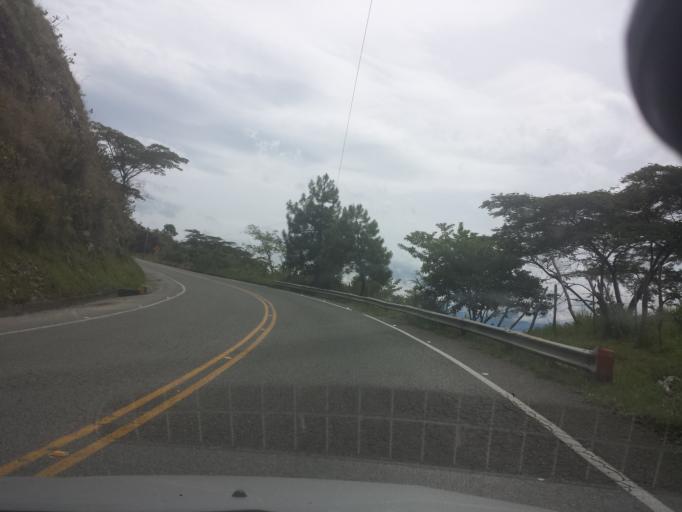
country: CO
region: Antioquia
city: Liborina
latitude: 6.6370
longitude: -75.8720
